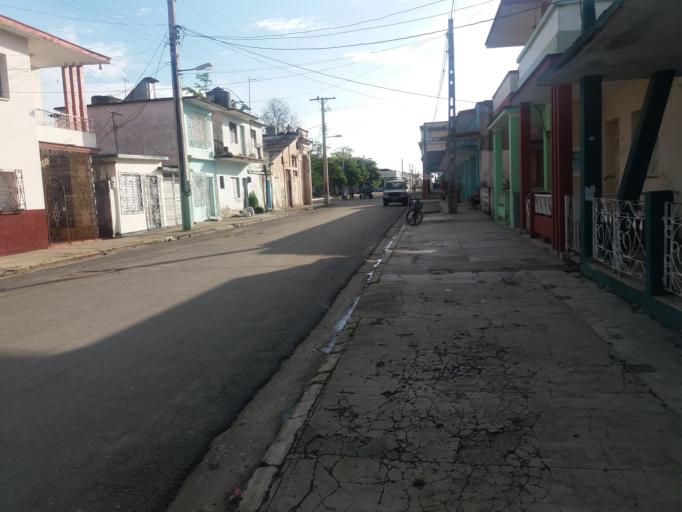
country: CU
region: Cienfuegos
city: Cruces
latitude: 22.3420
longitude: -80.2734
